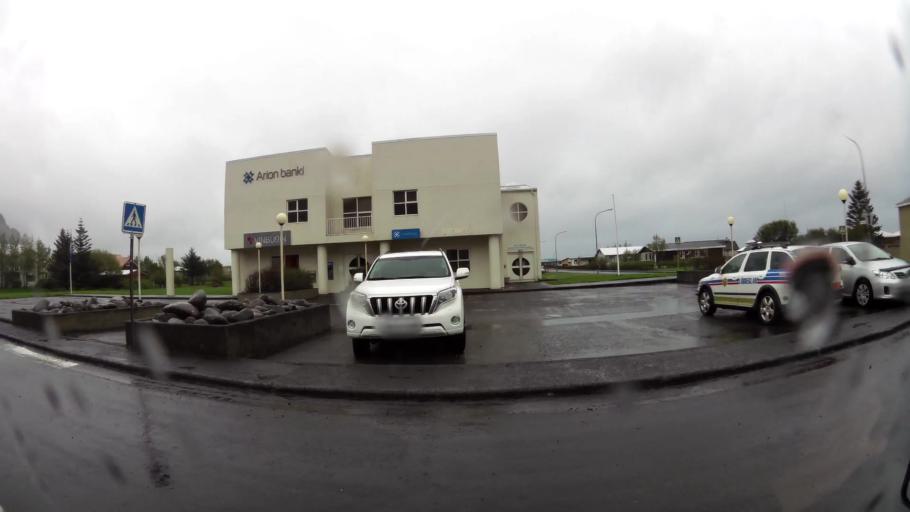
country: IS
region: South
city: Vestmannaeyjar
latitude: 63.4193
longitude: -19.0086
